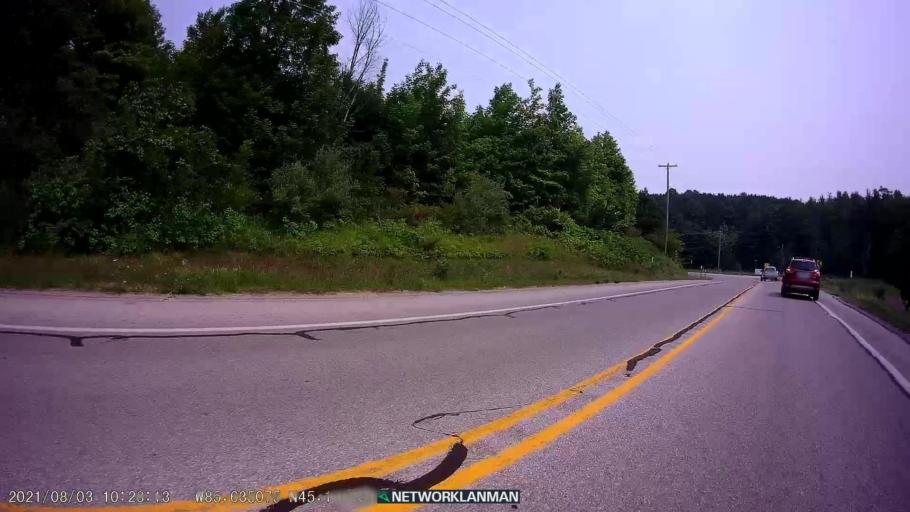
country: US
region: Michigan
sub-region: Leelanau County
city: Leland
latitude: 45.1102
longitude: -85.6348
